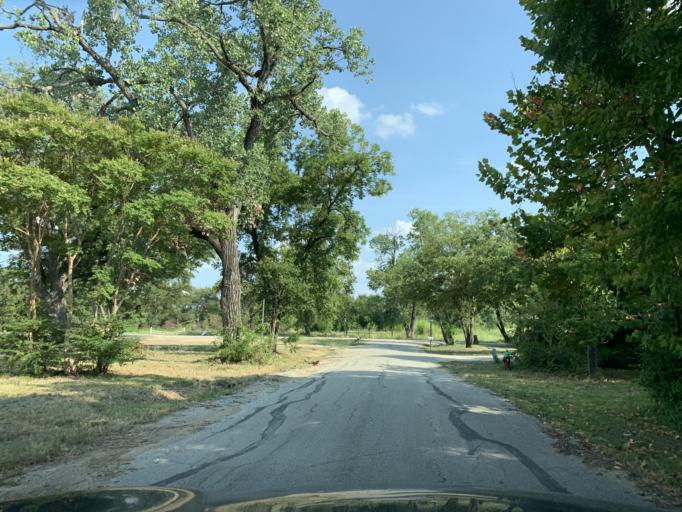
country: US
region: Texas
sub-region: Tarrant County
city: Haltom City
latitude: 32.7874
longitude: -97.2556
